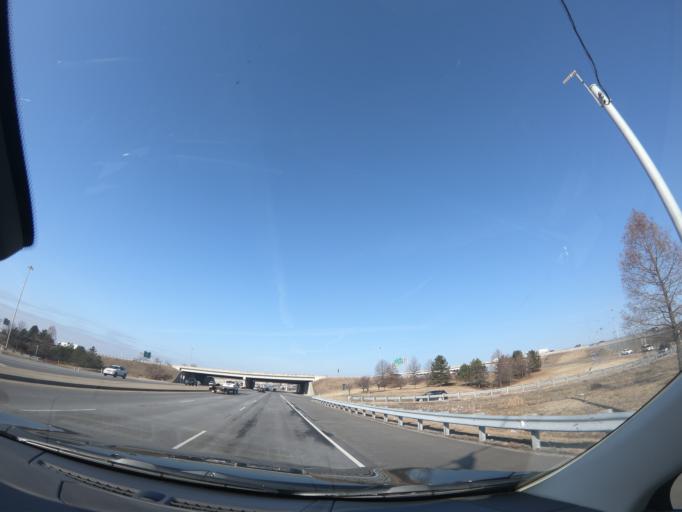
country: US
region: Kentucky
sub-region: Jefferson County
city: Beechwood Village
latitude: 38.2499
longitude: -85.6175
